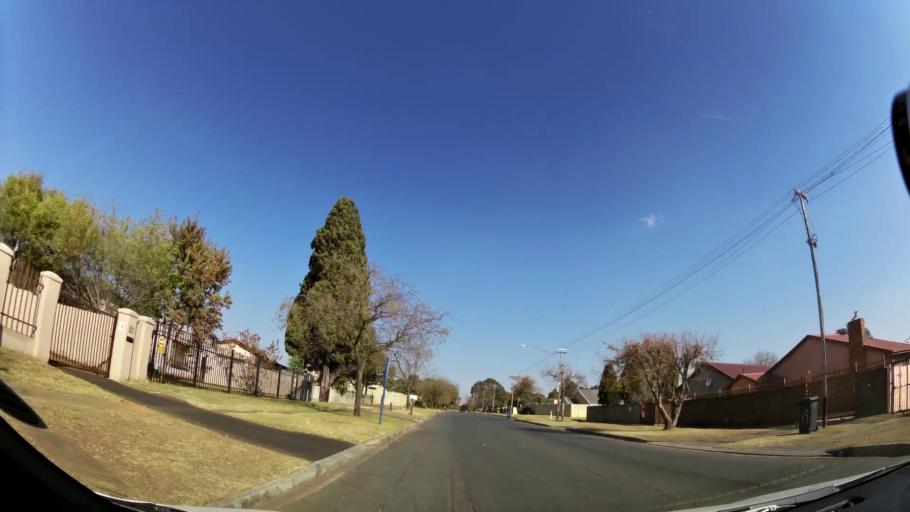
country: ZA
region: Gauteng
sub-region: City of Johannesburg Metropolitan Municipality
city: Johannesburg
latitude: -26.2538
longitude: 28.0035
